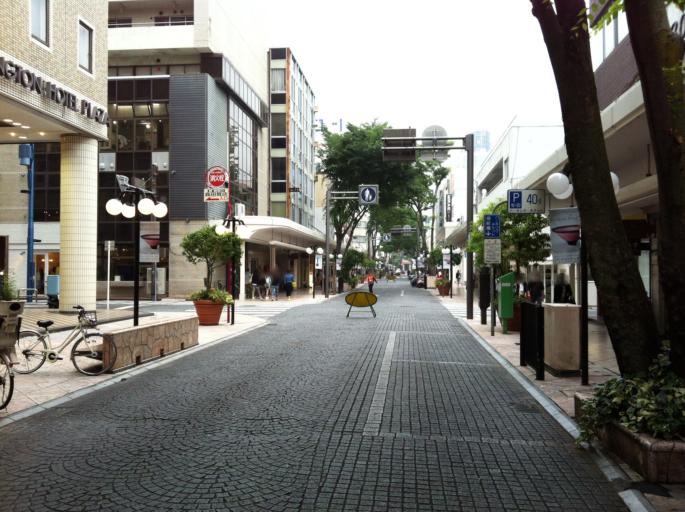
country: JP
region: Shizuoka
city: Shizuoka-shi
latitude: 34.9731
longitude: 138.3806
